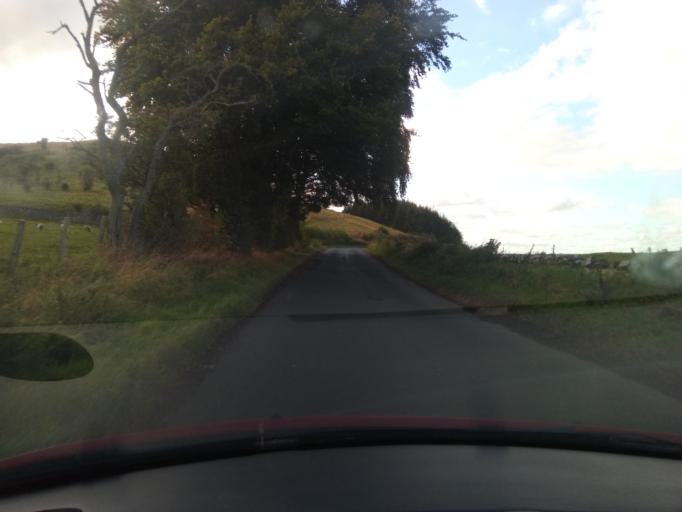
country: GB
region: Scotland
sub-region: The Scottish Borders
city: Kelso
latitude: 55.5200
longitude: -2.3301
